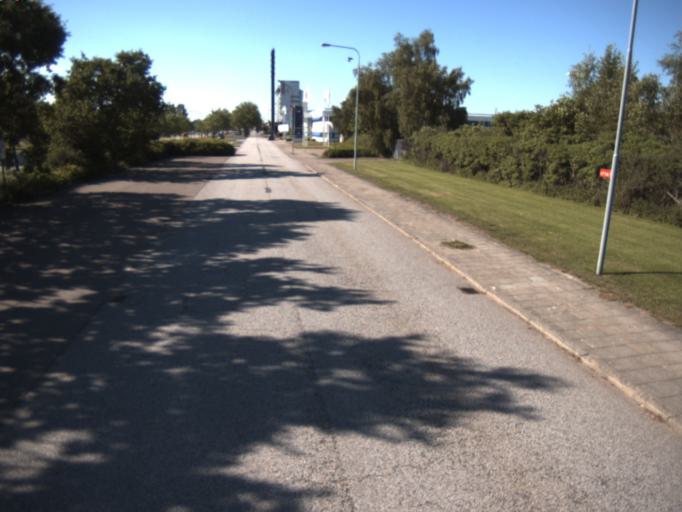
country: SE
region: Skane
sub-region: Helsingborg
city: Rydeback
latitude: 56.0062
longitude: 12.7386
